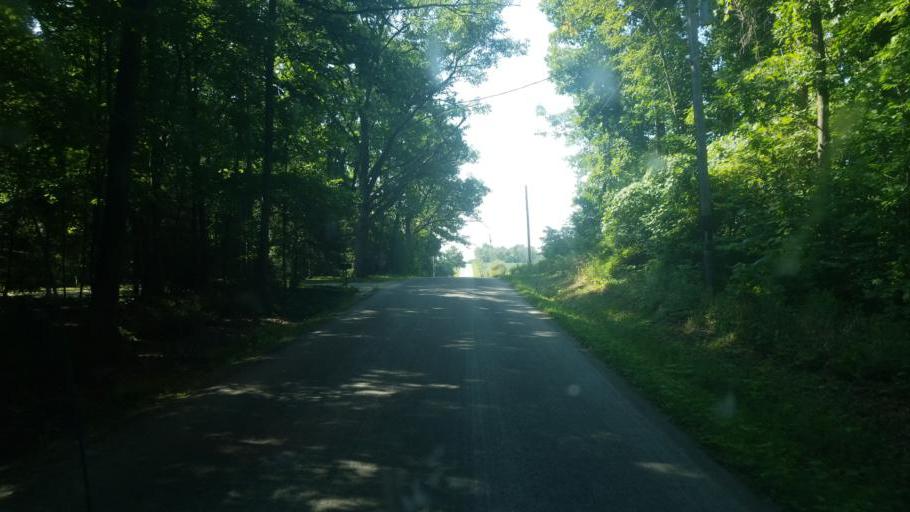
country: US
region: Ohio
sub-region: Lorain County
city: Wellington
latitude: 41.0627
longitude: -82.2016
